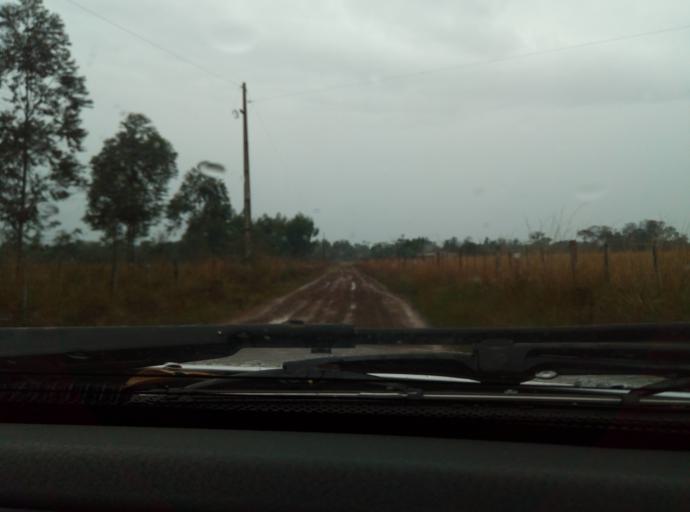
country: PY
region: Caaguazu
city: Carayao
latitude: -25.1036
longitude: -56.4173
